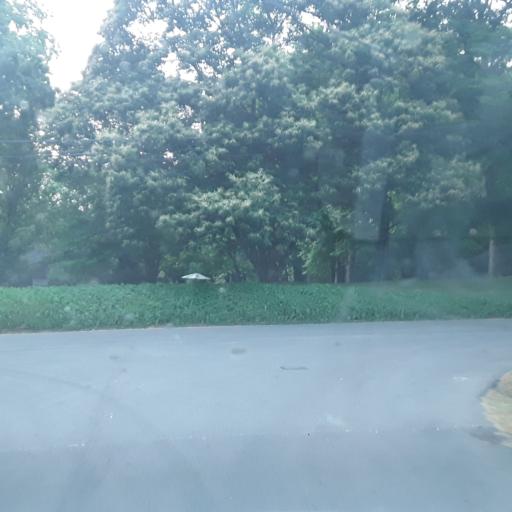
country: US
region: Tennessee
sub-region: Williamson County
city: Brentwood
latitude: 36.0523
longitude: -86.7638
